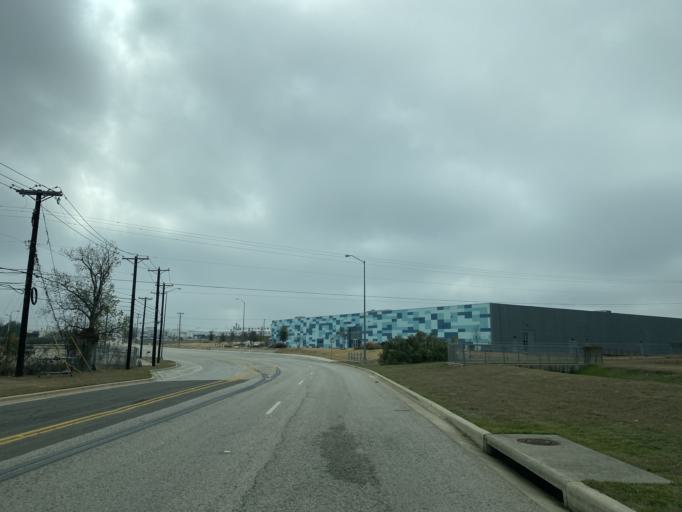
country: US
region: Texas
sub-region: Williamson County
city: Round Rock
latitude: 30.5395
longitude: -97.6888
